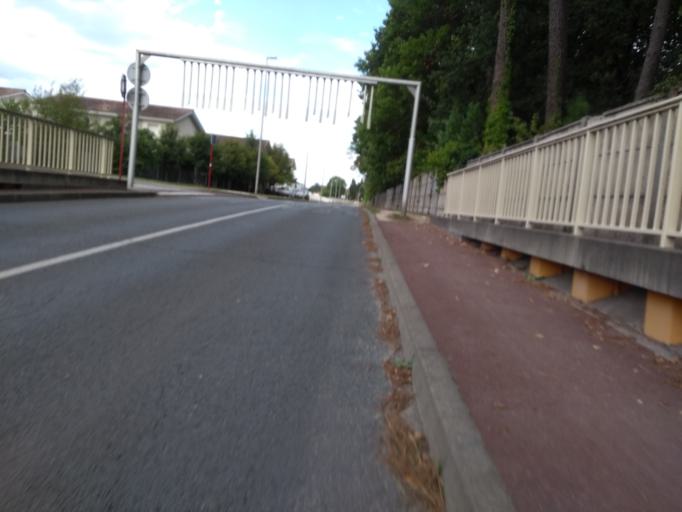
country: FR
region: Aquitaine
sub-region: Departement de la Gironde
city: Cestas
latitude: 44.7838
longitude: -0.6796
